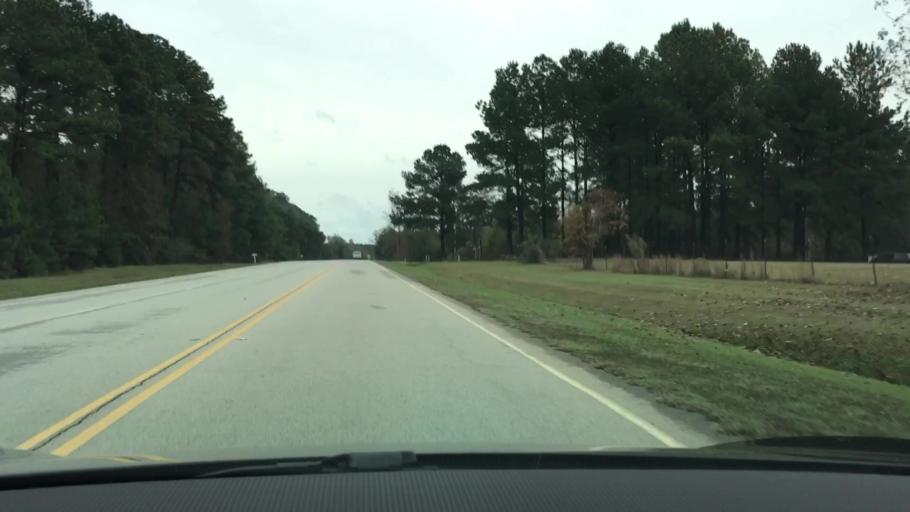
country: US
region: Georgia
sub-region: Warren County
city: Firing Range
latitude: 33.4792
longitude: -82.7431
